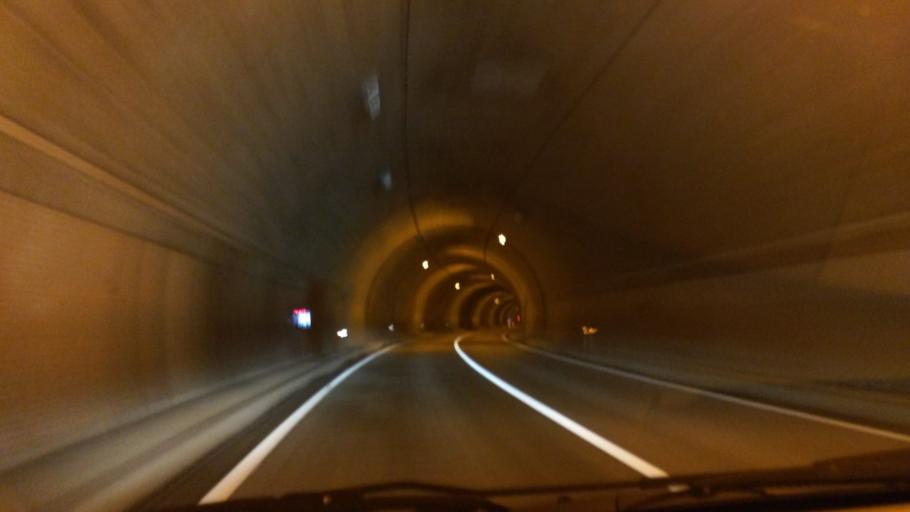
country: JP
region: Fukushima
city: Kitakata
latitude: 37.3596
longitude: 139.8720
